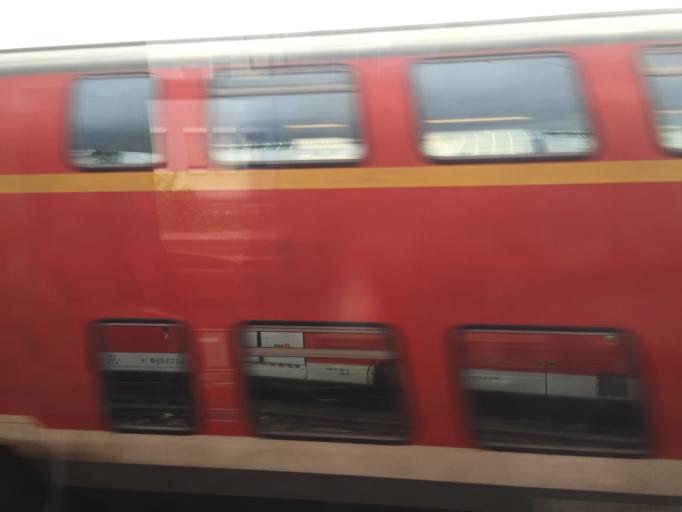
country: DE
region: Bavaria
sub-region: Regierungsbezirk Mittelfranken
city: Nuernberg
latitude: 49.4449
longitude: 11.0785
